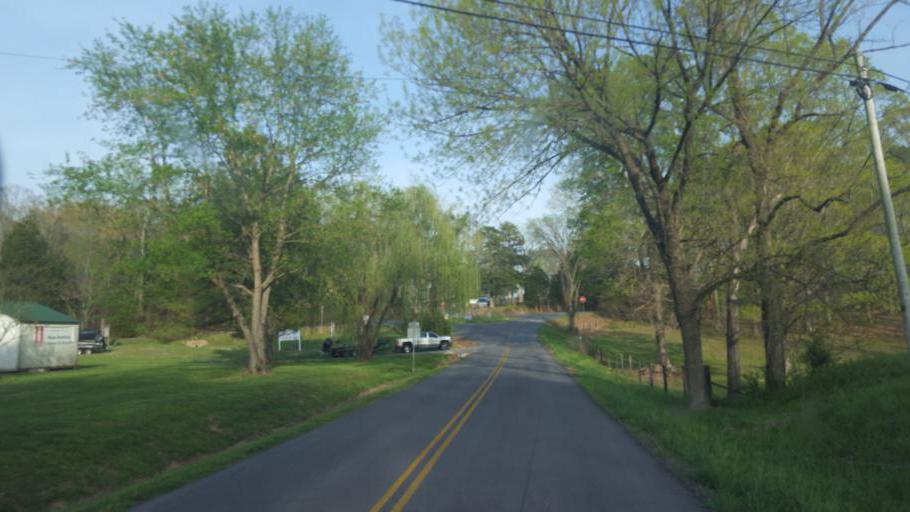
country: US
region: Kentucky
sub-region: Allen County
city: Scottsville
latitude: 36.8842
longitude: -86.1287
